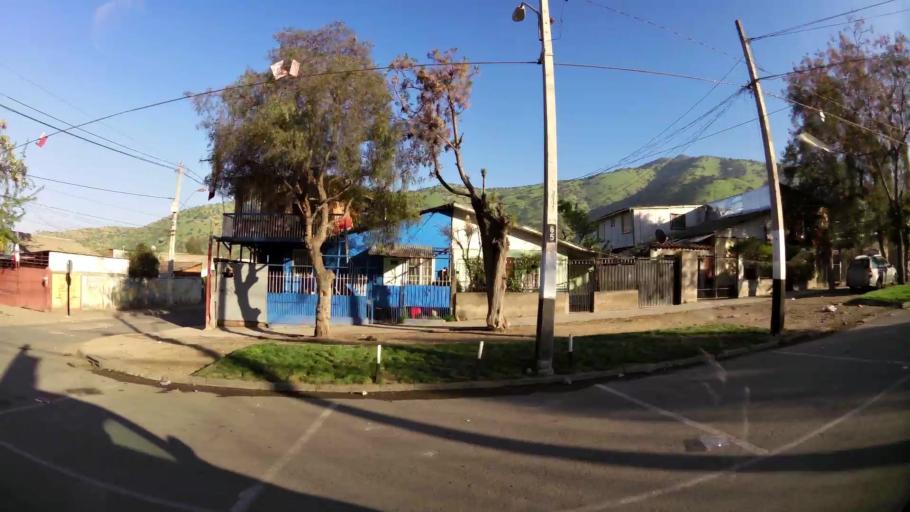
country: CL
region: Santiago Metropolitan
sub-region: Provincia de Chacabuco
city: Chicureo Abajo
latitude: -33.3639
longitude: -70.6296
